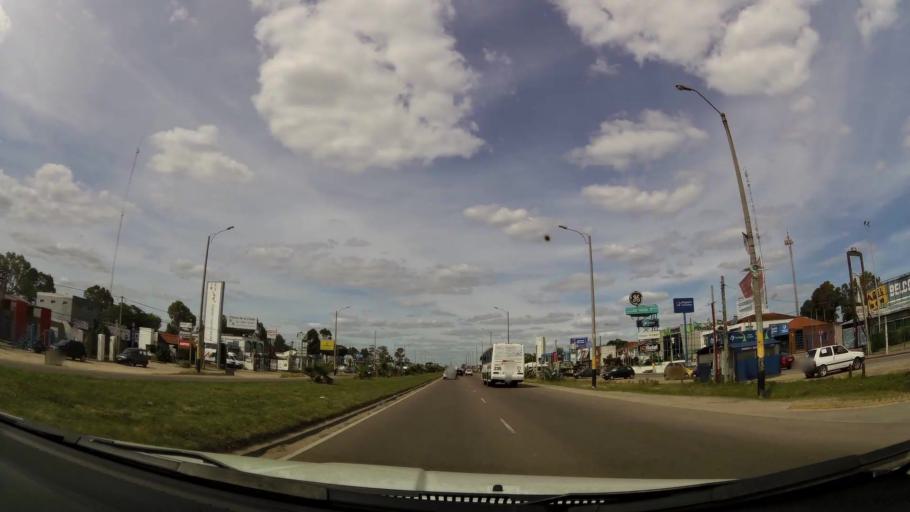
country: UY
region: Canelones
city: Barra de Carrasco
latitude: -34.8340
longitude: -55.9804
